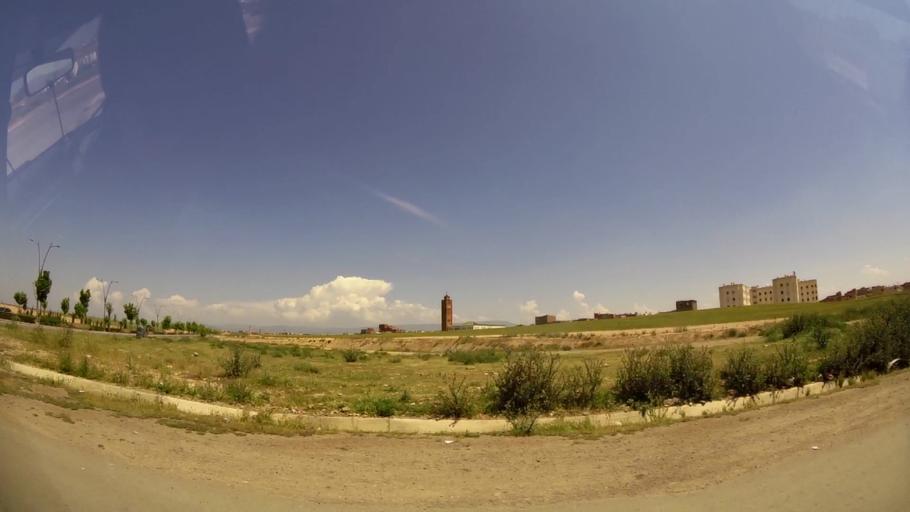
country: MA
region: Oriental
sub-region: Oujda-Angad
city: Oujda
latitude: 34.6972
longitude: -1.9408
